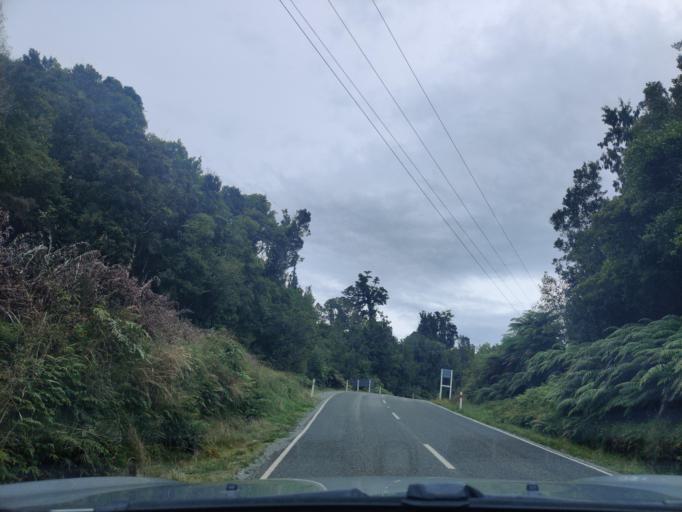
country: NZ
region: West Coast
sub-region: Westland District
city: Hokitika
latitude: -43.1740
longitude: 170.4578
